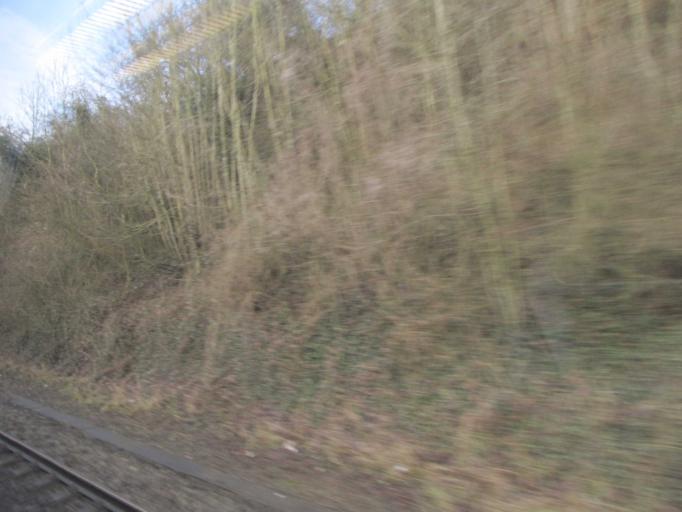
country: GB
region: England
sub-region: Hampshire
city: Basingstoke
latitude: 51.2720
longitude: -1.0734
